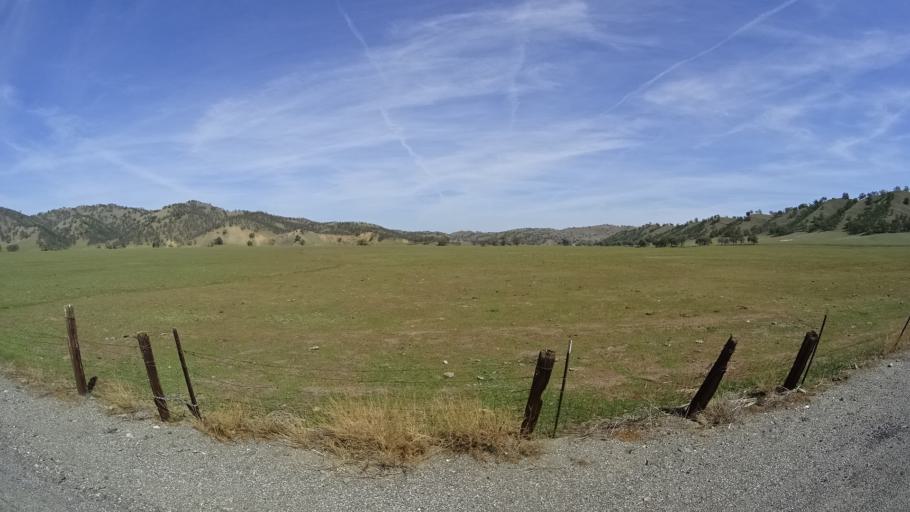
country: US
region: California
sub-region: Glenn County
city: Willows
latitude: 39.5377
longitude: -122.4438
